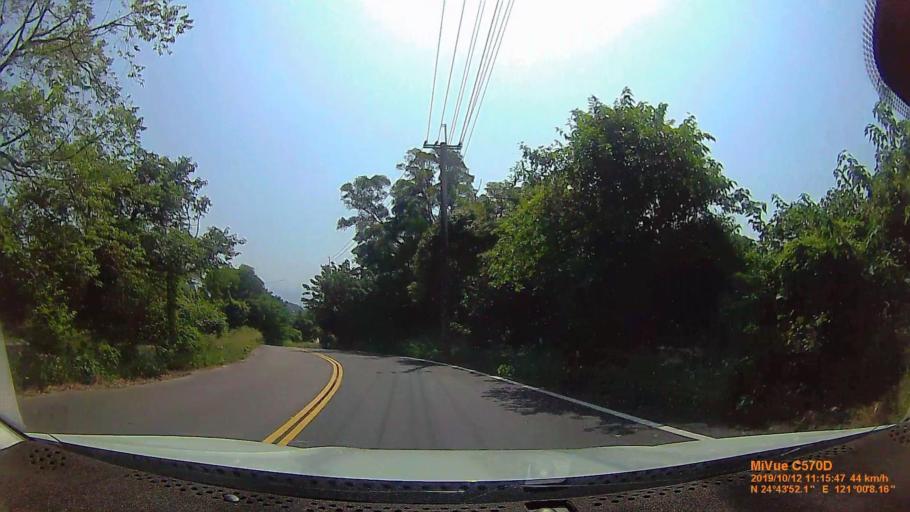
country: TW
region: Taiwan
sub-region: Hsinchu
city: Hsinchu
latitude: 24.7310
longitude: 121.0023
